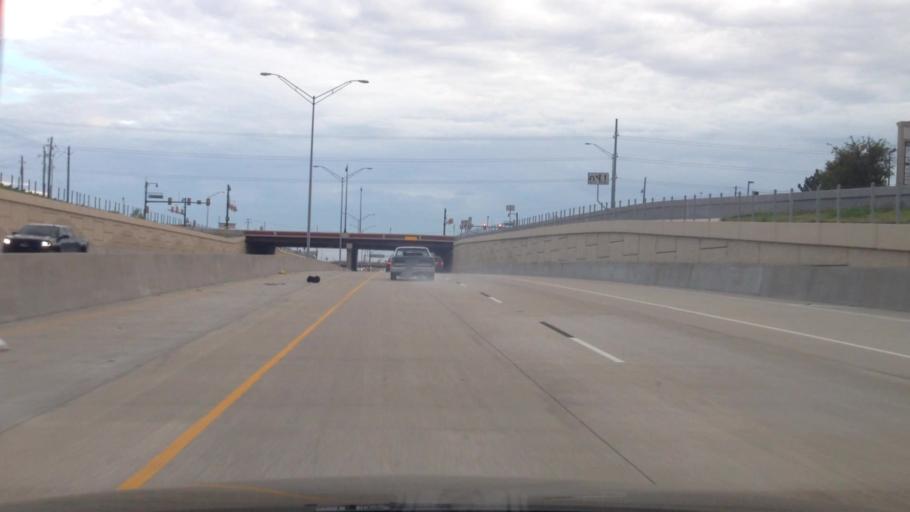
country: US
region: Texas
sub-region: Dallas County
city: Coppell
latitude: 32.9747
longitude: -97.0366
